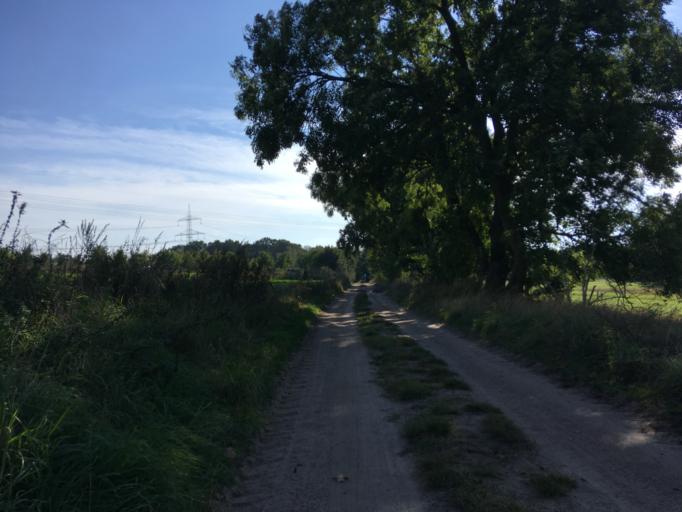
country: DE
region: Brandenburg
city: Altlandsberg
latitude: 52.5465
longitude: 13.7243
